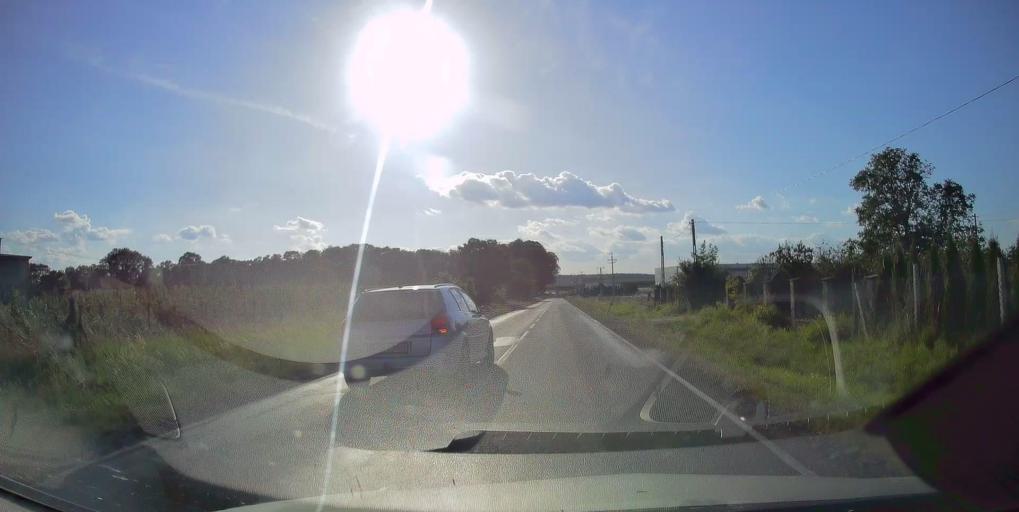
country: PL
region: Masovian Voivodeship
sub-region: Powiat grojecki
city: Bledow
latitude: 51.8138
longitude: 20.7449
